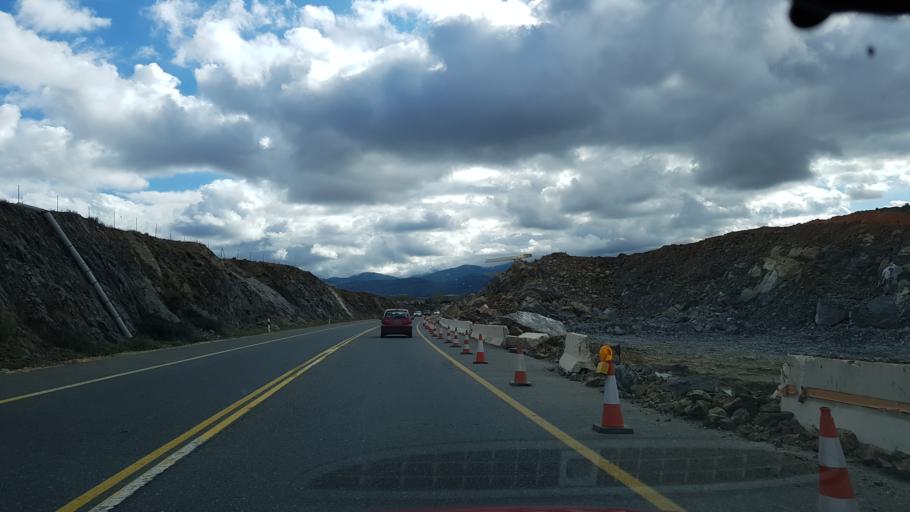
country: ES
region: Castille and Leon
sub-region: Provincia de Segovia
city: San Cristobal de Segovia
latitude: 40.9434
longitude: -4.0857
